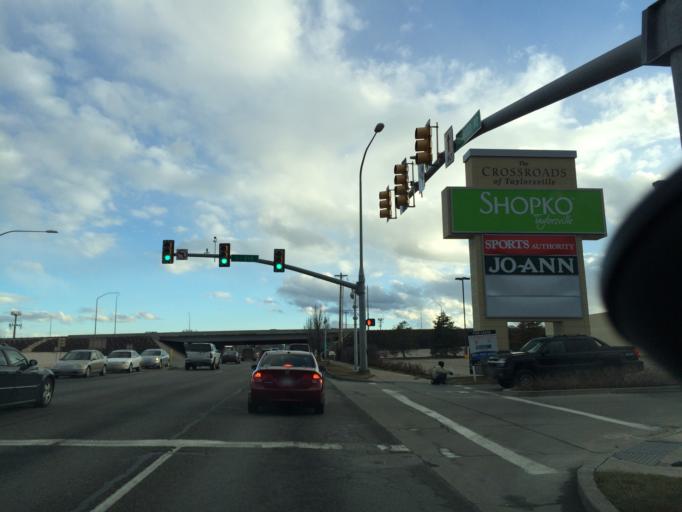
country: US
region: Utah
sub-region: Salt Lake County
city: Taylorsville
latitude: 40.6467
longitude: -111.9389
